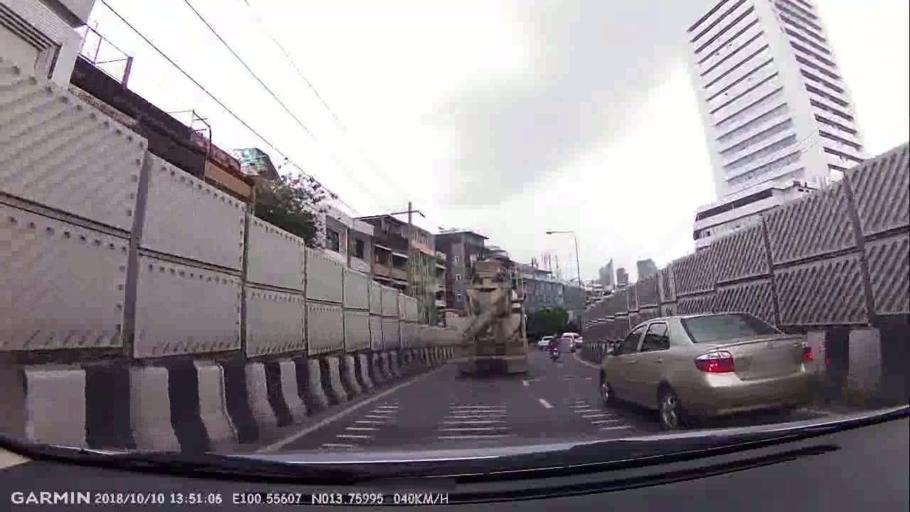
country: TH
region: Bangkok
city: Din Daeng
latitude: 13.7600
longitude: 100.5561
